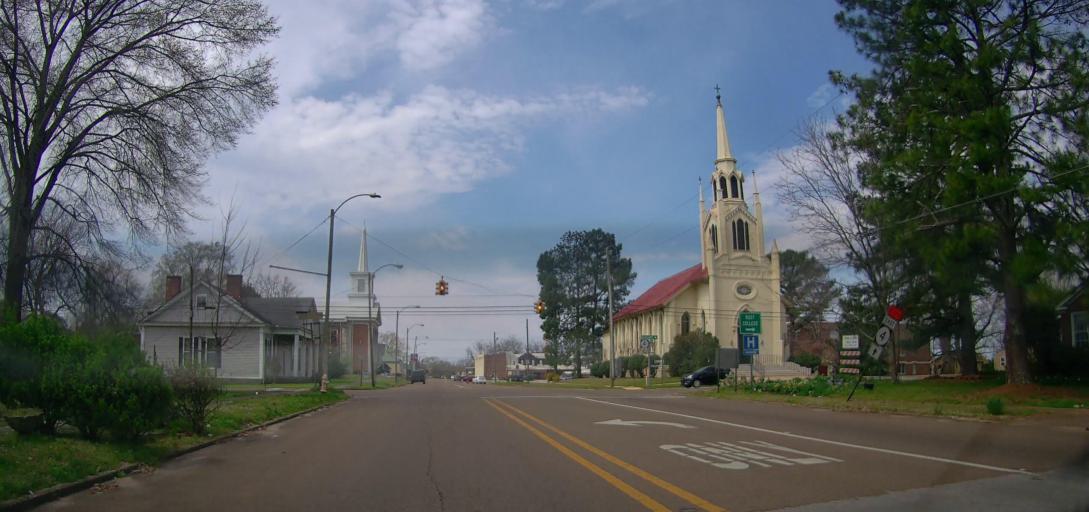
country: US
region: Mississippi
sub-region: Marshall County
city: Holly Springs
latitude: 34.7674
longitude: -89.4445
